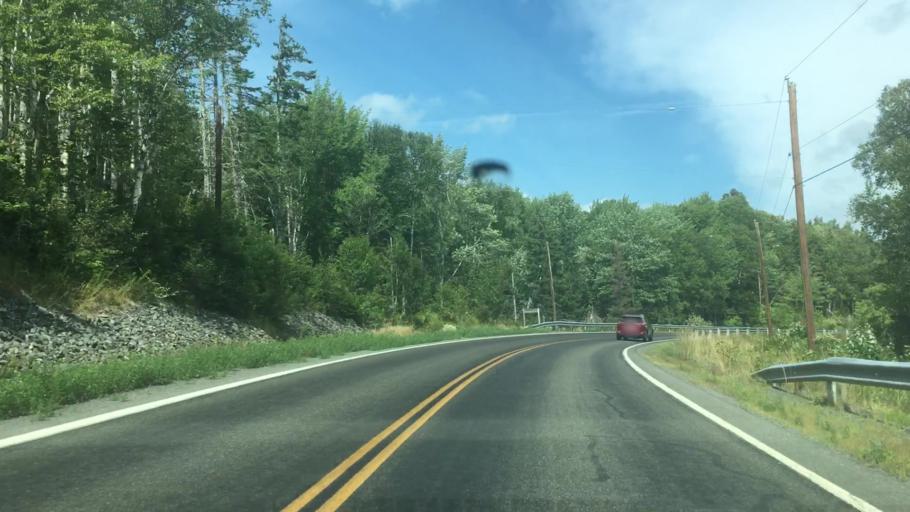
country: CA
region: Nova Scotia
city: Sydney Mines
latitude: 46.2139
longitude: -60.6201
